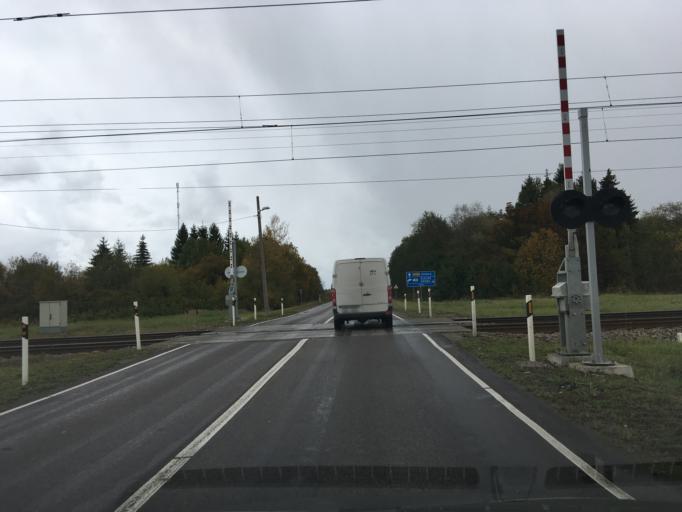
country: EE
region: Harju
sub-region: Anija vald
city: Kehra
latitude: 59.3435
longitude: 25.3116
